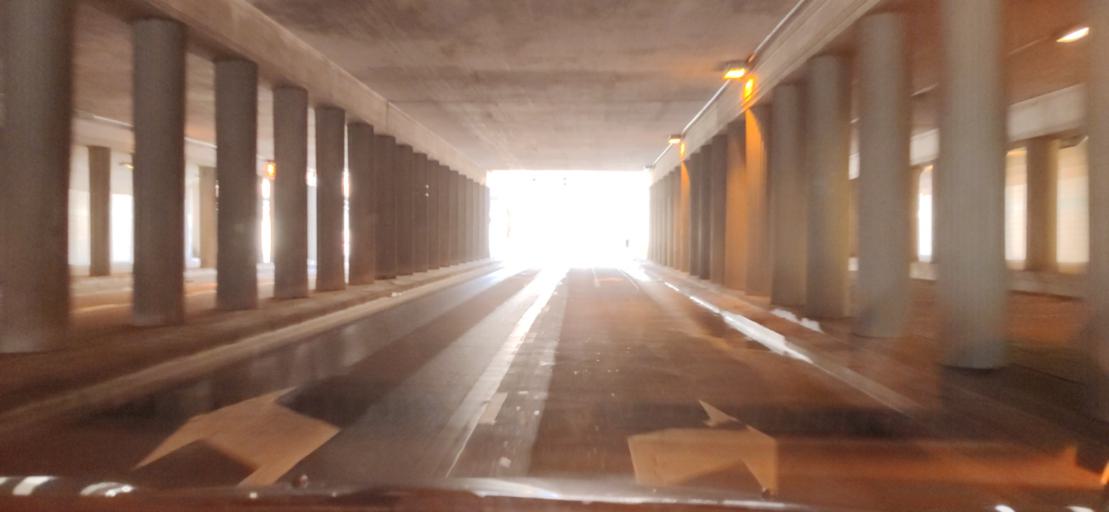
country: NL
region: Overijssel
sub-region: Gemeente Hengelo
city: Hengelo
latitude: 52.2618
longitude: 6.7923
